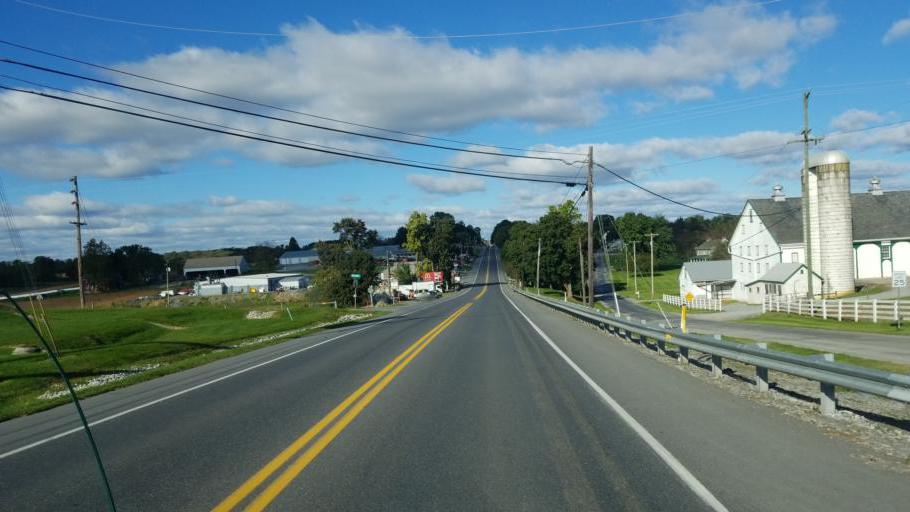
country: US
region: Pennsylvania
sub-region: Franklin County
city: Waynesboro
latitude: 39.7637
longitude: -77.6050
